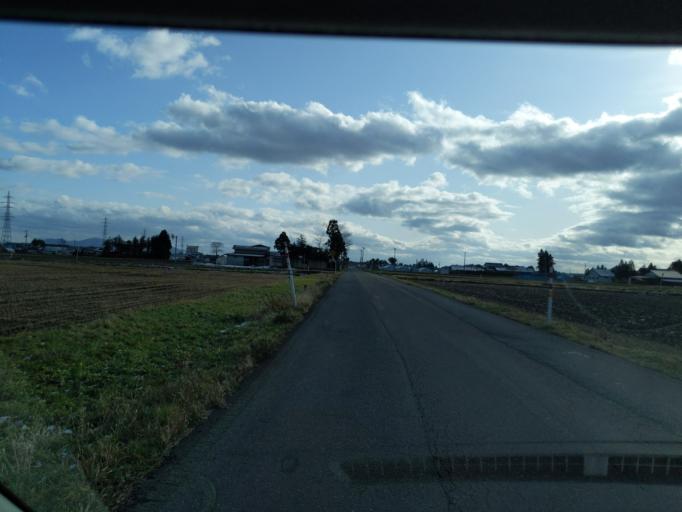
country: JP
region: Iwate
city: Mizusawa
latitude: 39.1505
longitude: 141.0783
